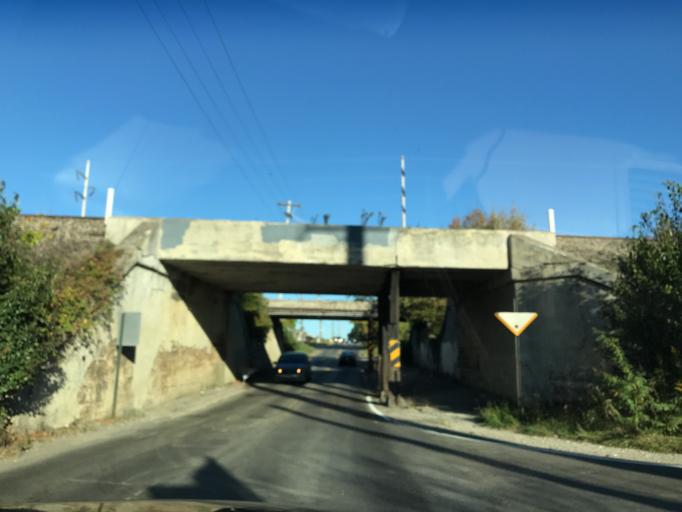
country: US
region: Ohio
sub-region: Franklin County
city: Worthington
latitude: 40.1363
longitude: -83.0059
